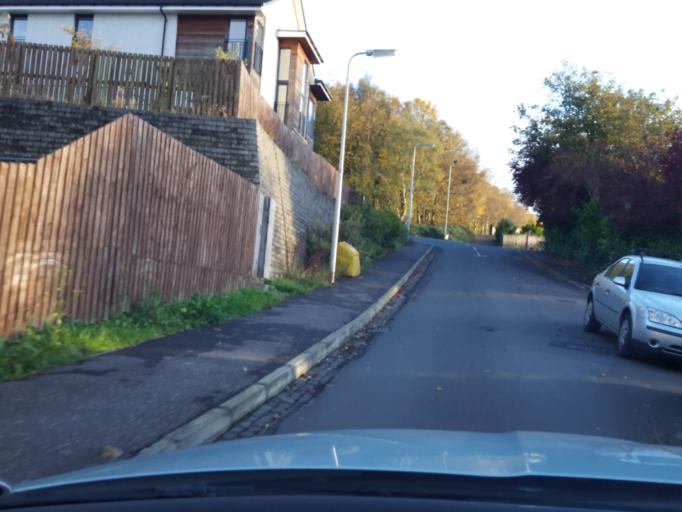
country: GB
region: Scotland
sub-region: Dundee City
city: Dundee
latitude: 56.4716
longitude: -2.9923
